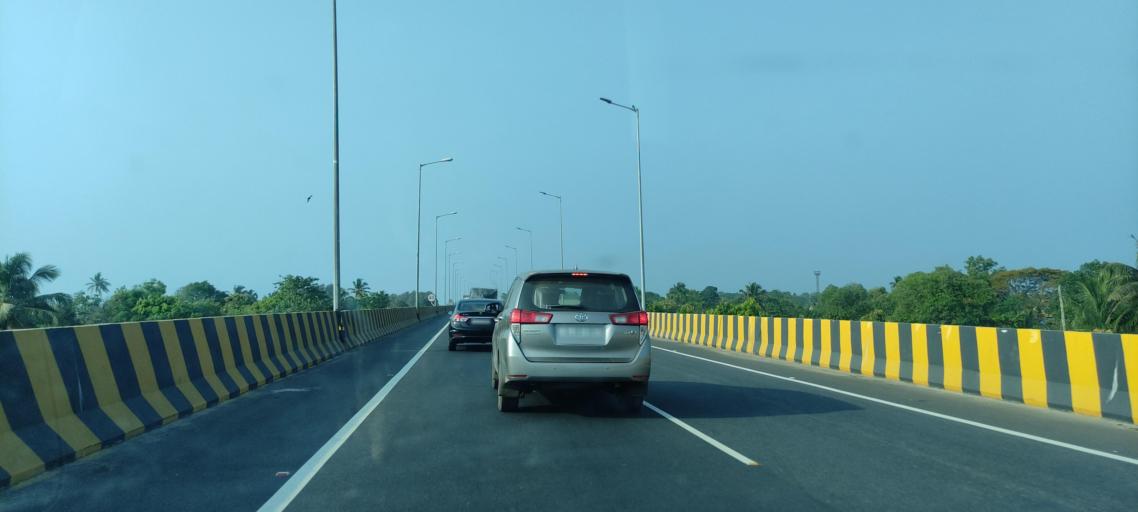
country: IN
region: Kerala
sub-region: Alappuzha
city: Alleppey
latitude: 9.4822
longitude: 76.3212
